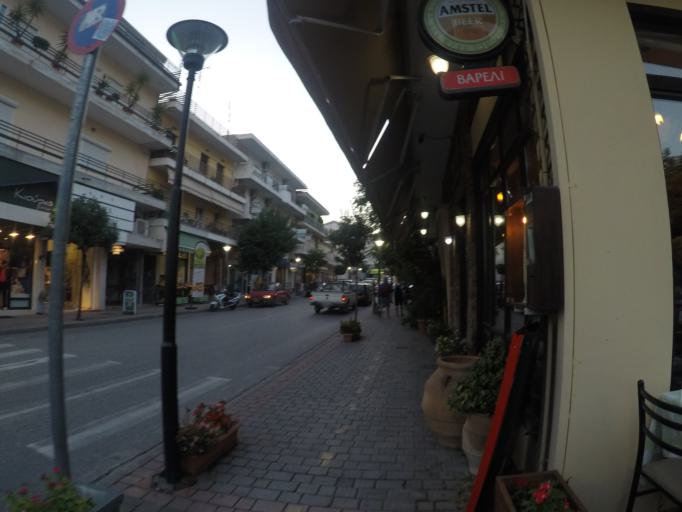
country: GR
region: Thessaly
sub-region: Trikala
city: Kalampaka
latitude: 39.7058
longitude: 21.6255
